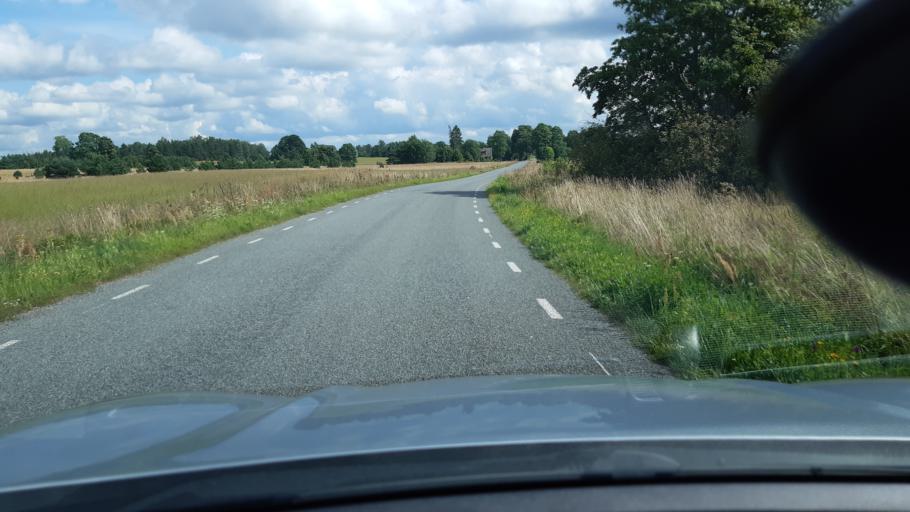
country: EE
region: Raplamaa
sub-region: Kehtna vald
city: Kehtna
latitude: 58.9091
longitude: 25.1182
